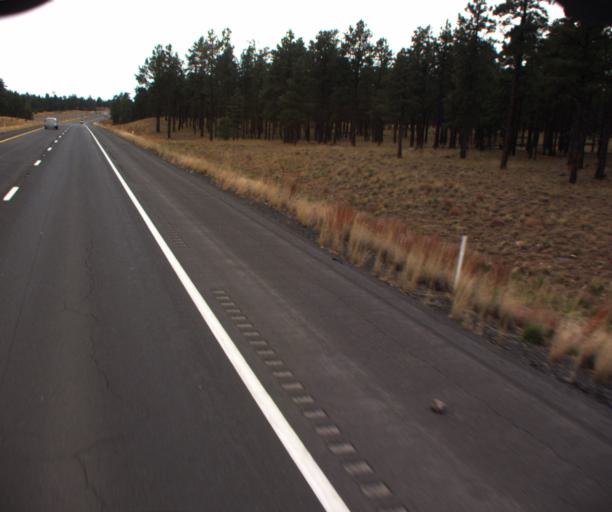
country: US
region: Arizona
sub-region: Coconino County
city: Flagstaff
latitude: 35.3690
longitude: -111.5743
